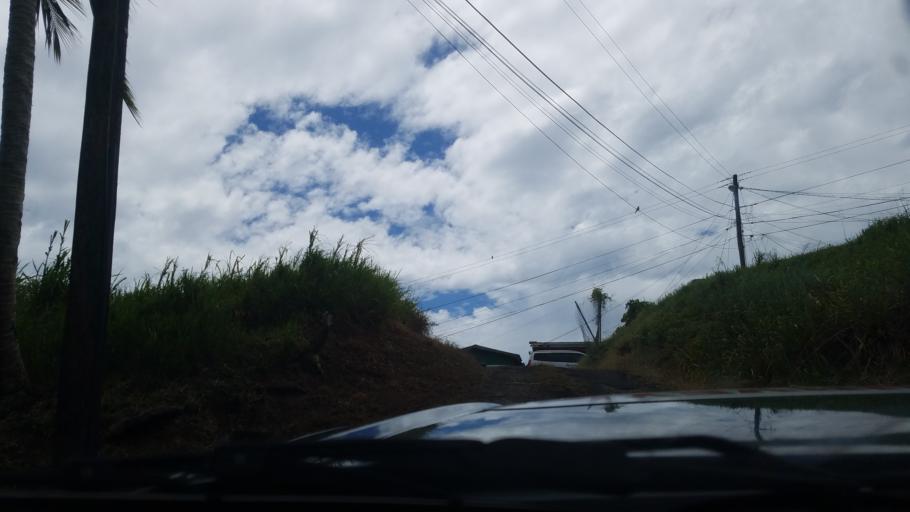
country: LC
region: Castries Quarter
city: Bisee
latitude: 14.0028
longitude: -60.9716
